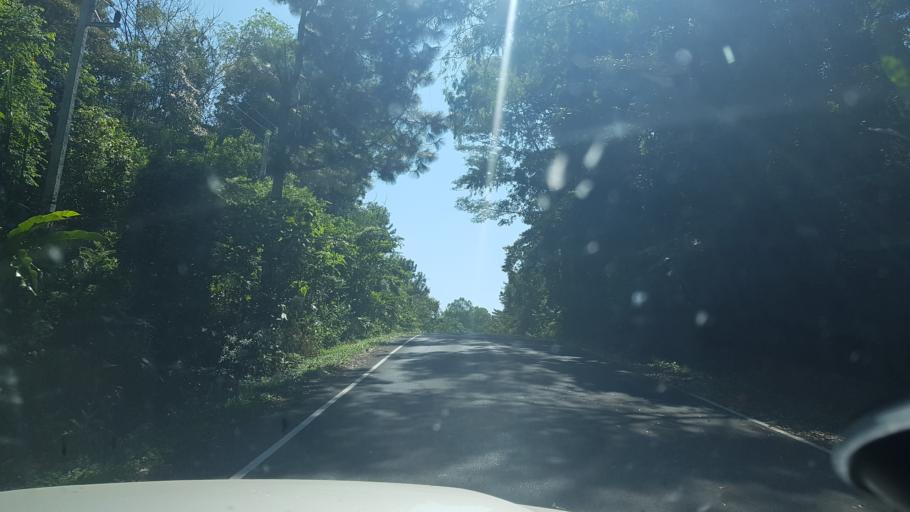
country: TH
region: Phetchabun
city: Khao Kho
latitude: 16.5559
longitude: 100.9803
